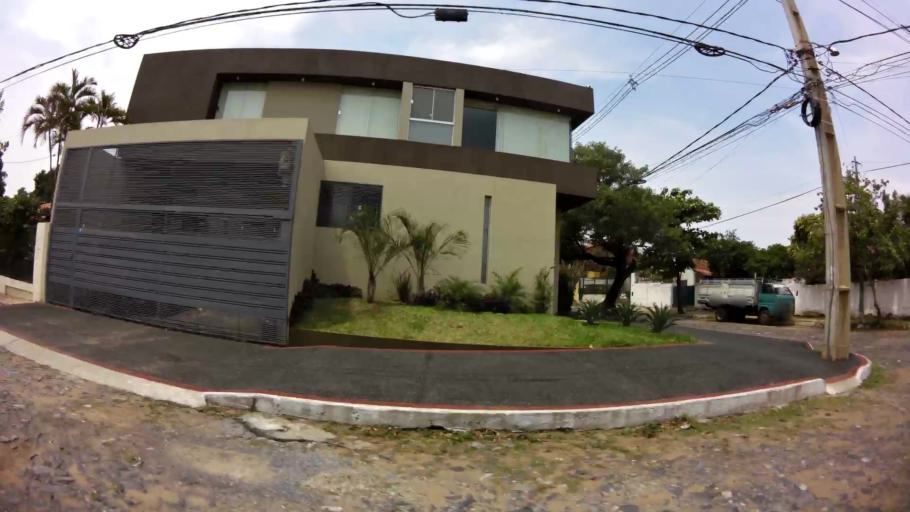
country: PY
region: Asuncion
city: Asuncion
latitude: -25.2689
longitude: -57.5951
